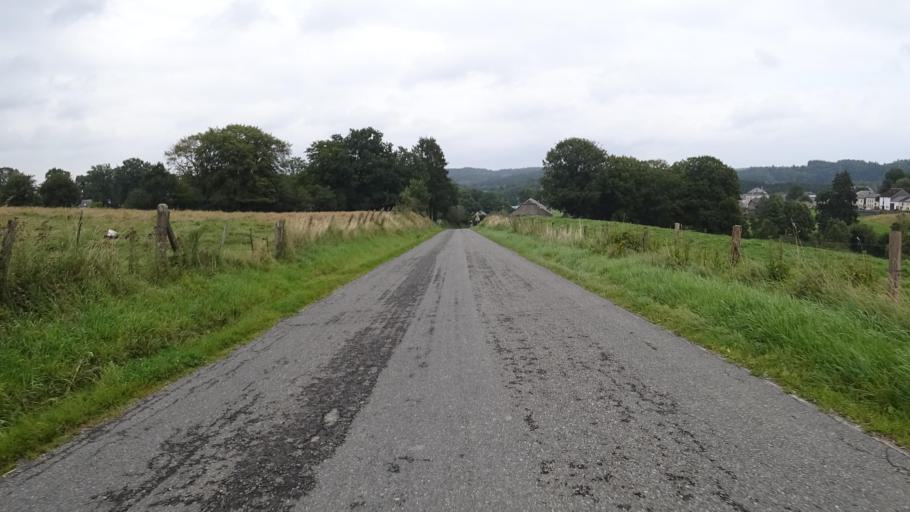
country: BE
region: Wallonia
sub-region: Province du Luxembourg
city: Chiny
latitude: 49.8056
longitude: 5.3549
